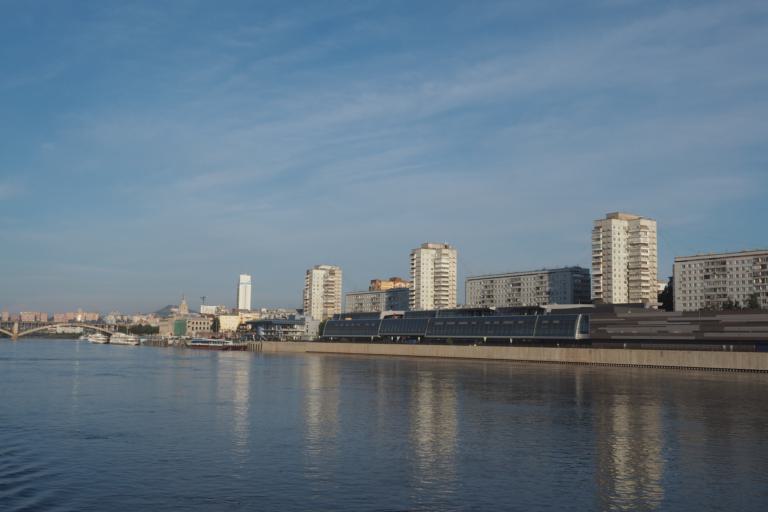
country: RU
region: Krasnoyarskiy
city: Krasnoyarsk
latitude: 56.0087
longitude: 92.8963
